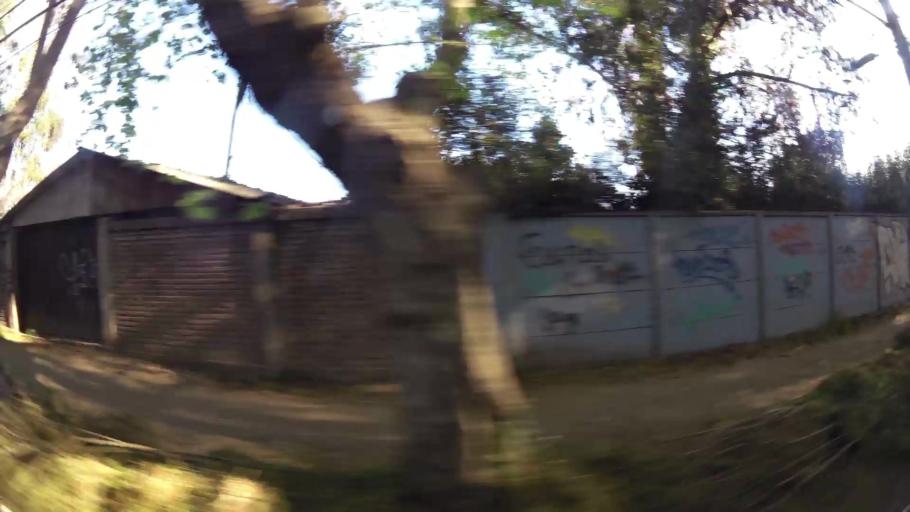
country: CL
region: Santiago Metropolitan
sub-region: Provincia de Talagante
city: Penaflor
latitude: -33.6003
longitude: -70.8667
